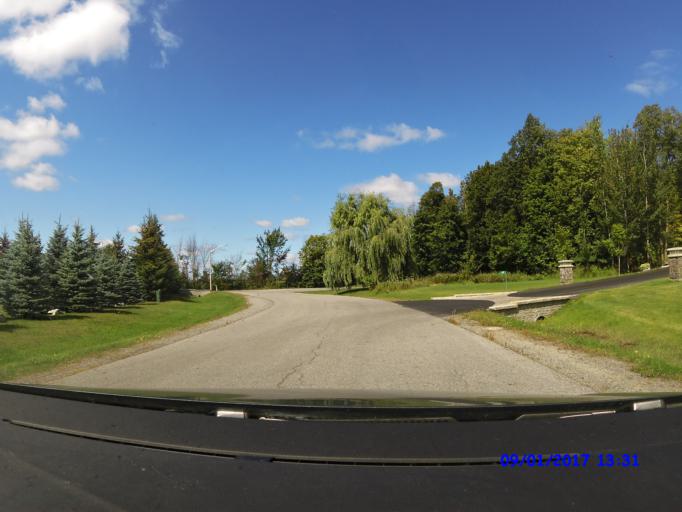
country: CA
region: Ontario
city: Bells Corners
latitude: 45.3580
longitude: -75.9904
